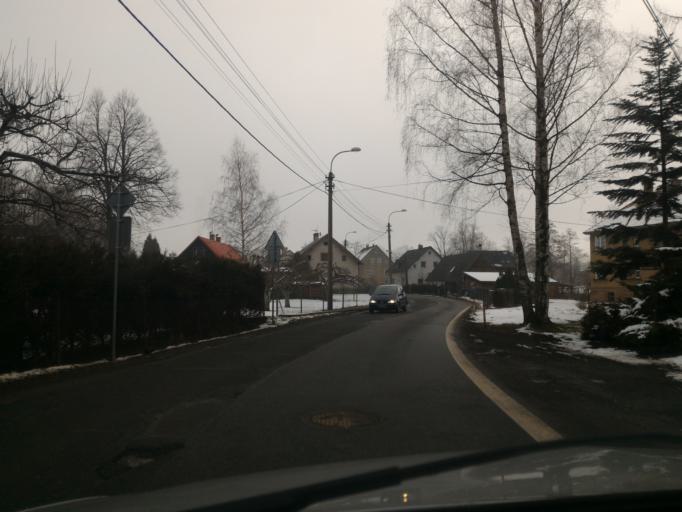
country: CZ
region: Liberecky
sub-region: Okres Liberec
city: Hejnice
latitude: 50.8758
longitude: 15.1940
